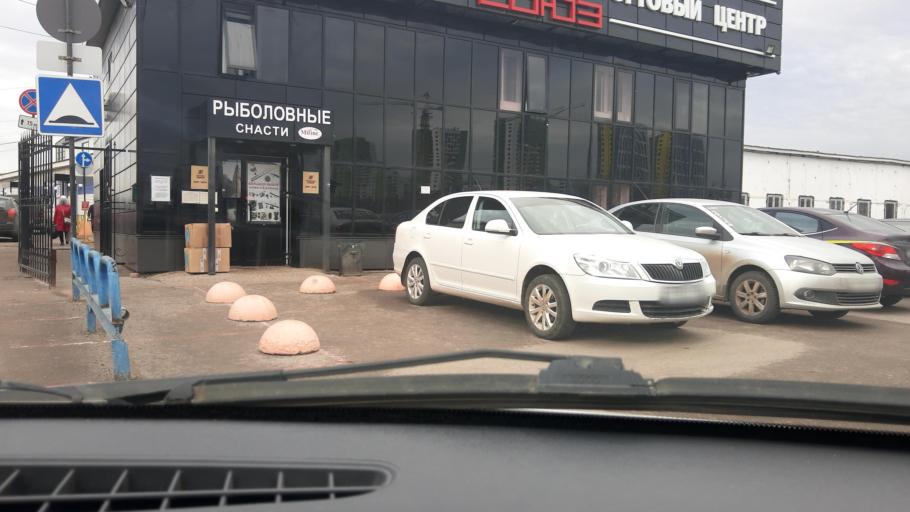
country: RU
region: Bashkortostan
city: Mikhaylovka
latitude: 54.6947
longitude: 55.8488
